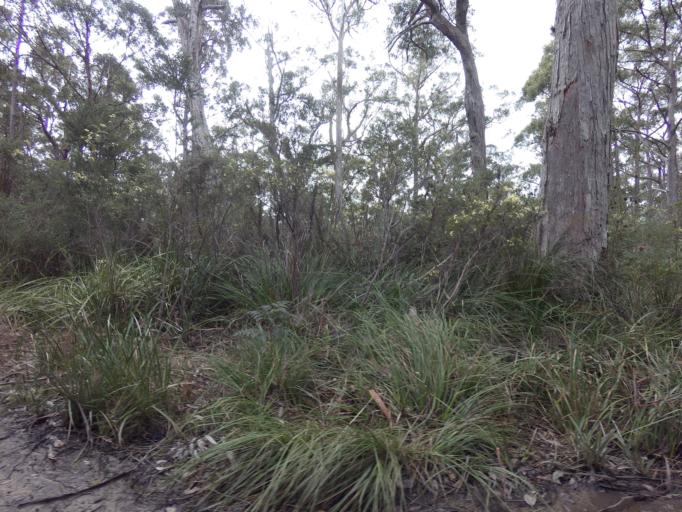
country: AU
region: Tasmania
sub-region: Huon Valley
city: Geeveston
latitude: -43.4668
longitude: 146.9308
